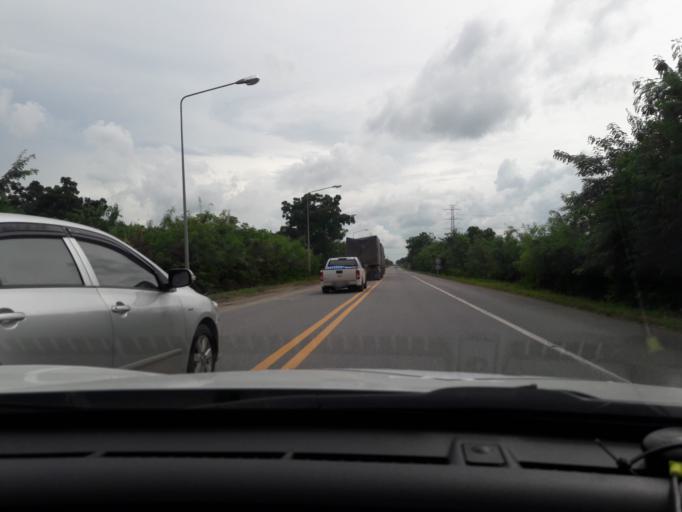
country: TH
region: Nakhon Sawan
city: Tak Fa
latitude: 15.4169
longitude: 100.5156
